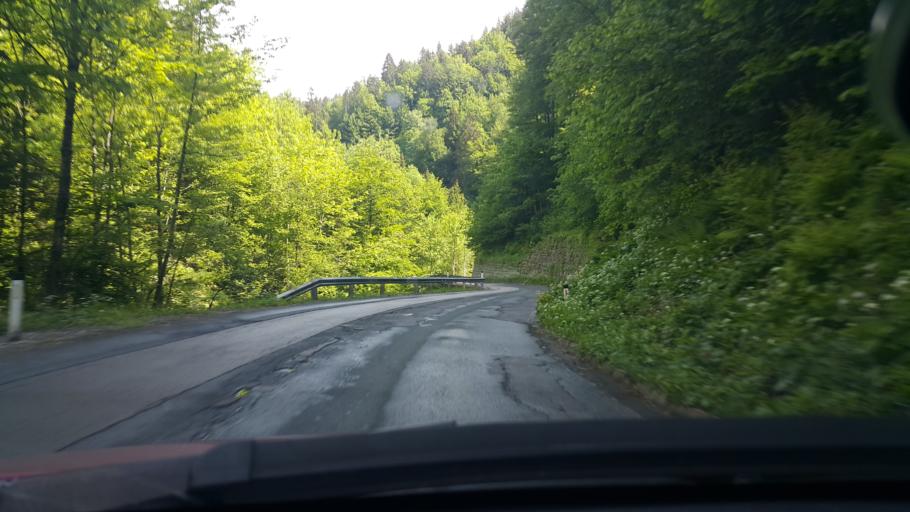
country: AT
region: Carinthia
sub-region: Politischer Bezirk Klagenfurt Land
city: Ferlach
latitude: 46.4710
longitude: 14.2584
